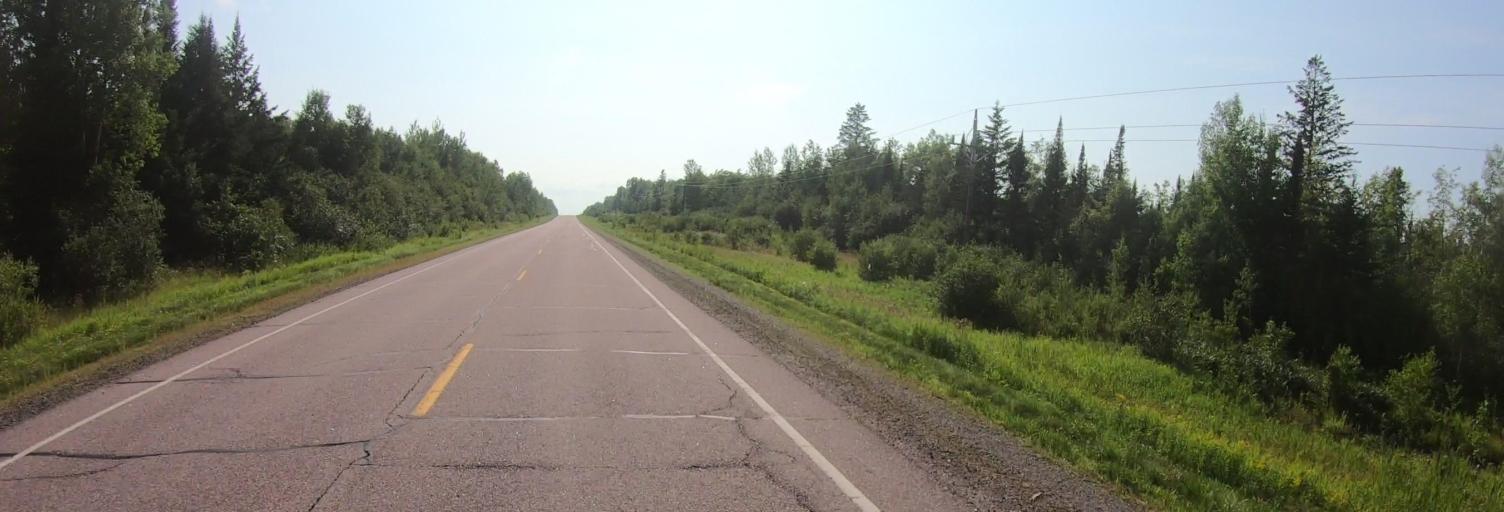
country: US
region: Wisconsin
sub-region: Iron County
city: Hurley
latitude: 46.3643
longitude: -90.4367
